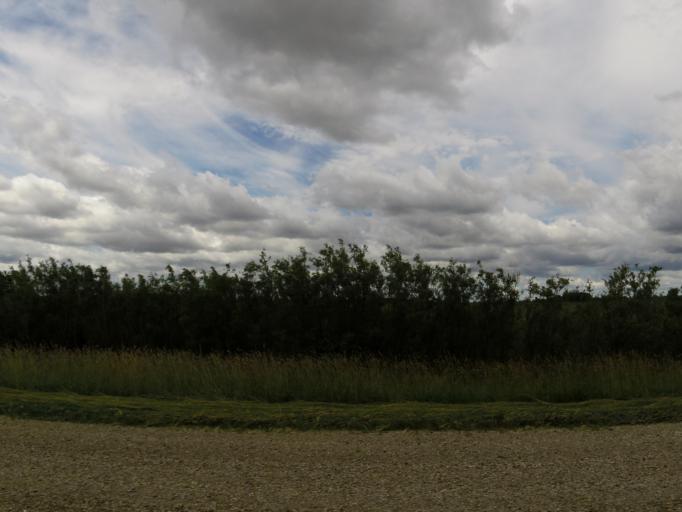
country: US
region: Iowa
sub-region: Howard County
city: Cresco
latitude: 43.4555
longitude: -92.2988
